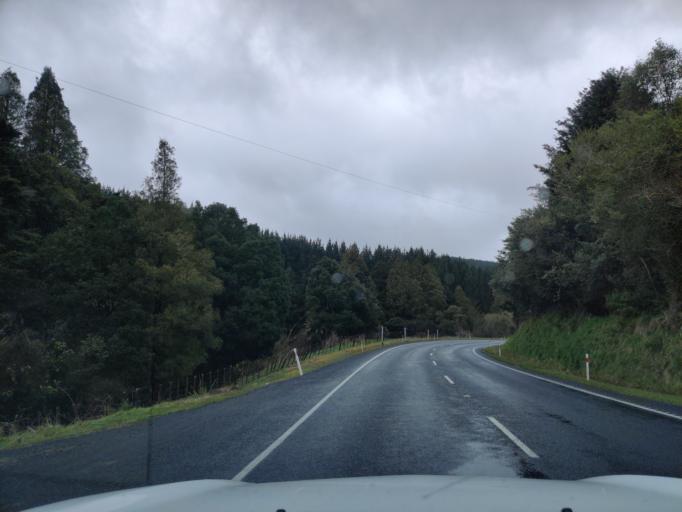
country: NZ
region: Waikato
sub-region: Otorohanga District
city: Otorohanga
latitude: -38.6601
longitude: 175.2063
